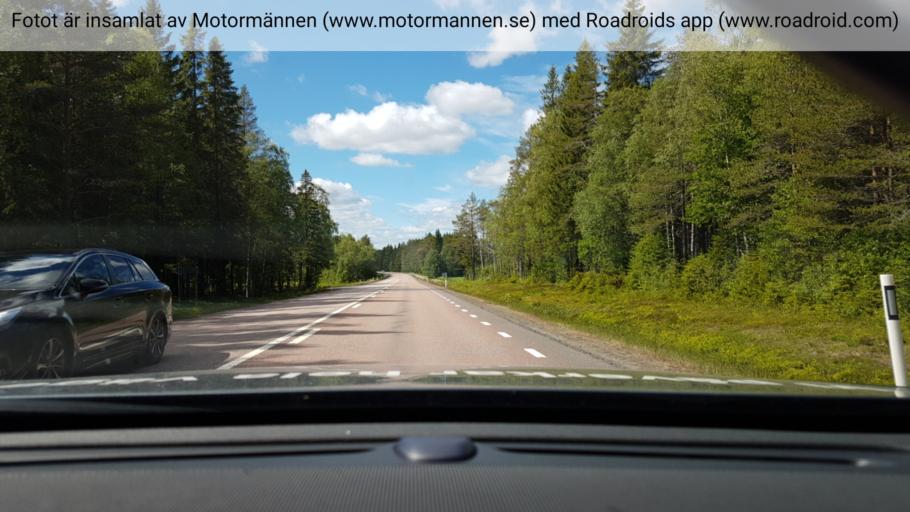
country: SE
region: Vaesterbotten
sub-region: Skelleftea Kommun
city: Burea
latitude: 64.3338
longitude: 21.2596
